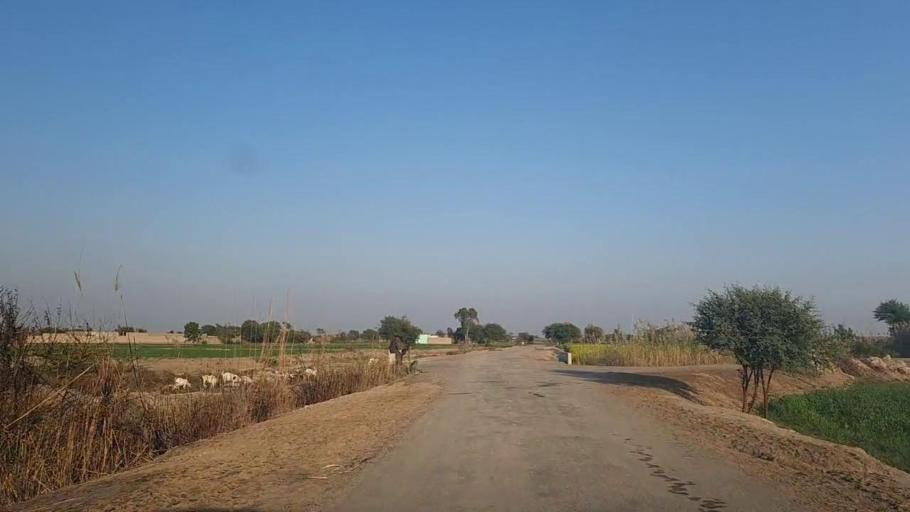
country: PK
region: Sindh
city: Jam Sahib
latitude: 26.3487
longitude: 68.6734
